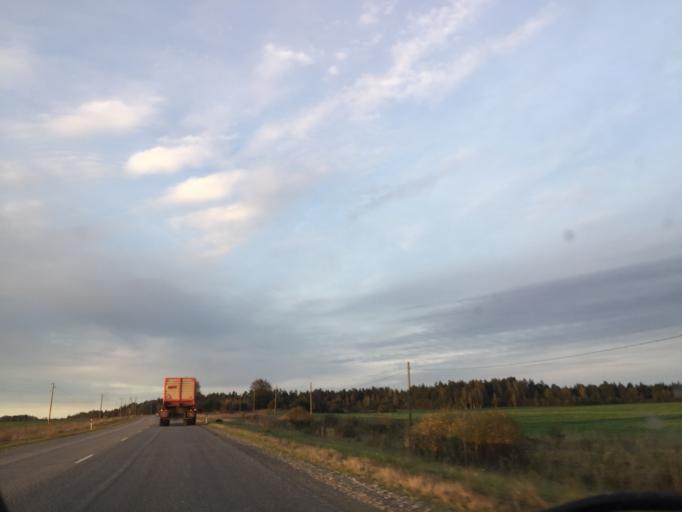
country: LV
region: Dobeles Rajons
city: Dobele
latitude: 56.7496
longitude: 23.3910
